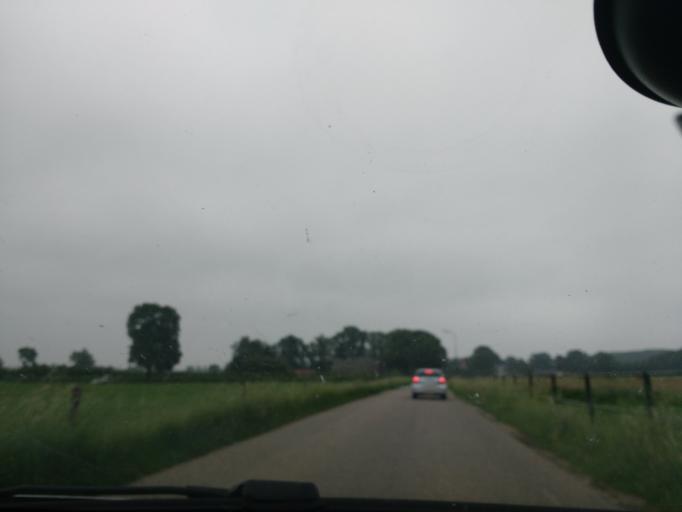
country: NL
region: Utrecht
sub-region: Gemeente Rhenen
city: Rhenen
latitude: 51.9664
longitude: 5.5934
